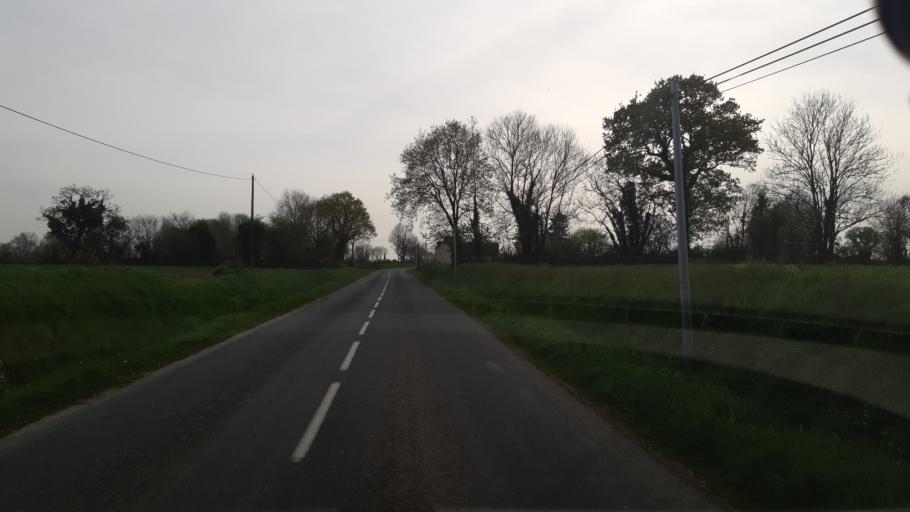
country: FR
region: Lower Normandy
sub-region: Departement de la Manche
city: Hambye
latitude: 48.9586
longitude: -1.3076
